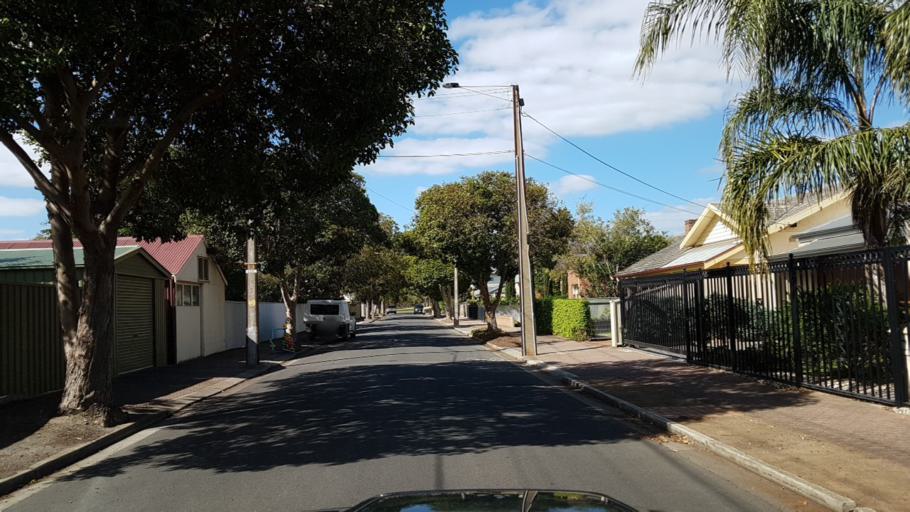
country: AU
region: South Australia
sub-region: Holdfast Bay
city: Glenelg East
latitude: -34.9710
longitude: 138.5223
